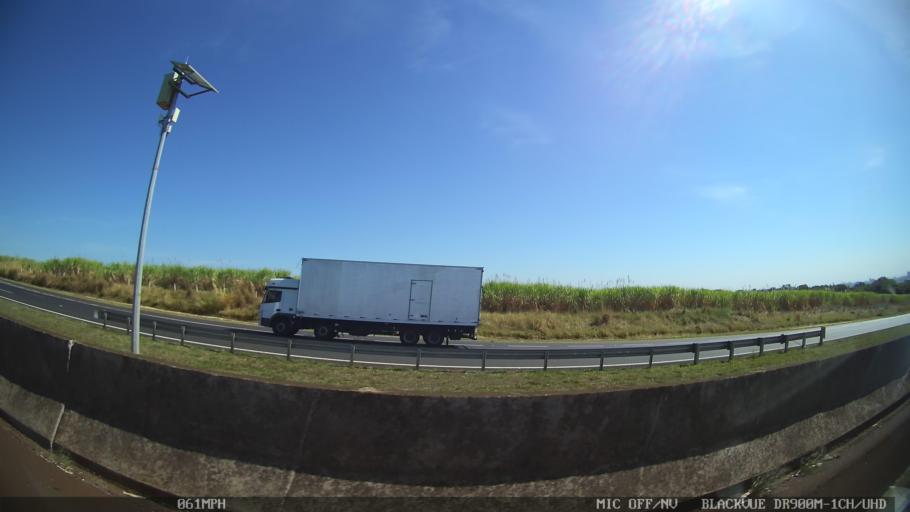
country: BR
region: Sao Paulo
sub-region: Cravinhos
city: Cravinhos
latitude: -21.2597
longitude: -47.7543
